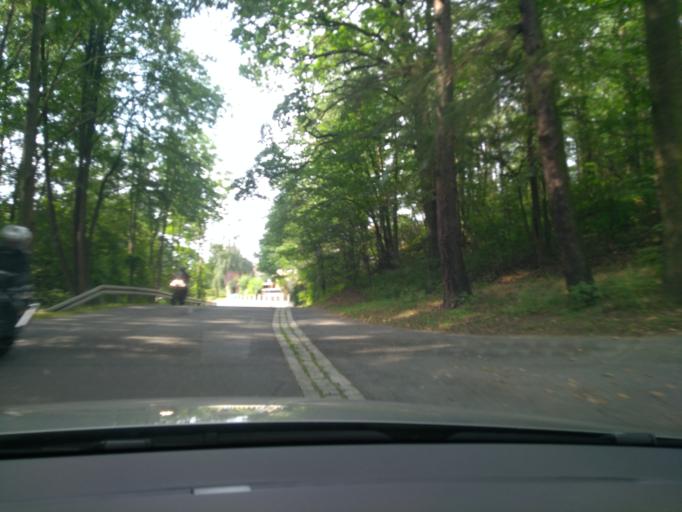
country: DE
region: Saxony
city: Markersdorf
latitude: 51.1420
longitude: 14.8761
